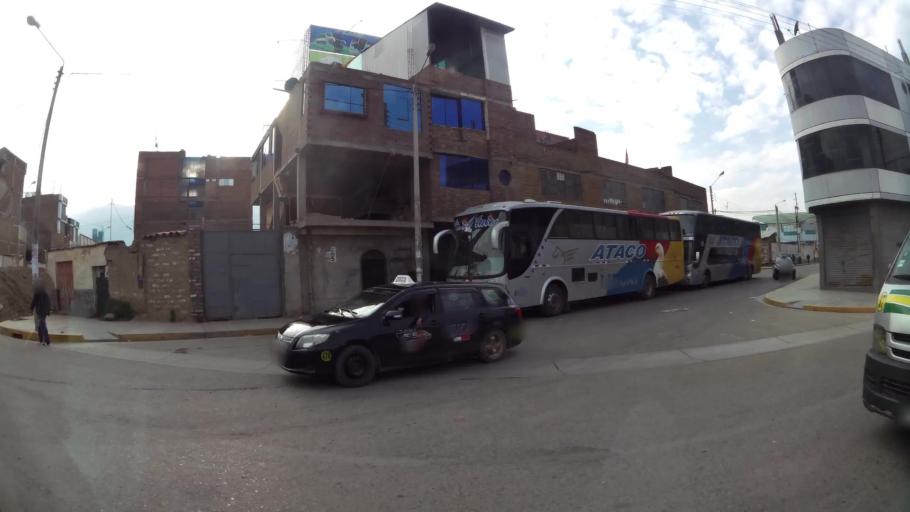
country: PE
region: Junin
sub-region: Provincia de Huancayo
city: Huancayo
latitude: -12.0751
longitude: -75.2046
